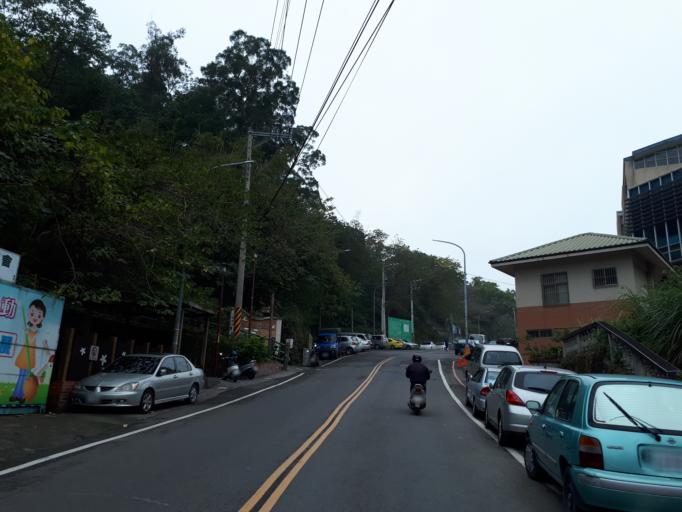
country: TW
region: Taiwan
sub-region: Hsinchu
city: Zhubei
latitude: 24.7348
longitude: 121.0861
